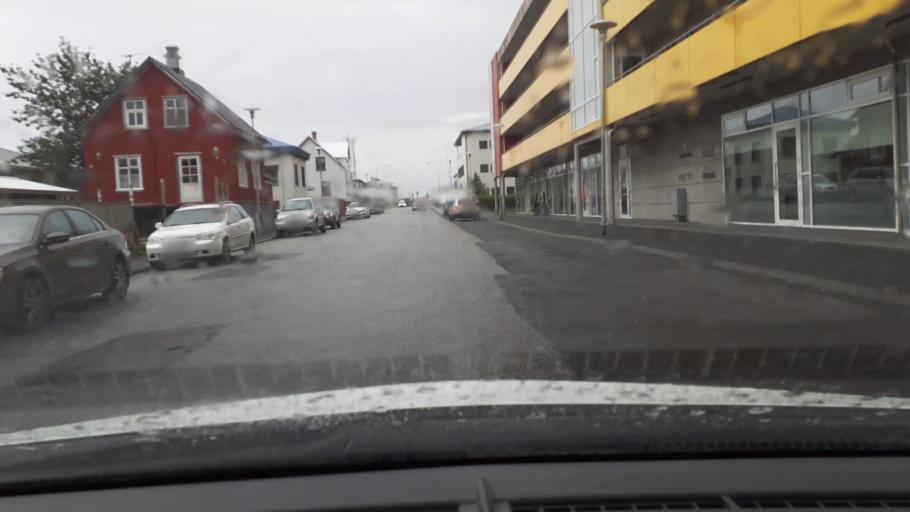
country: IS
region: West
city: Akranes
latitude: 64.3180
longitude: -22.0818
